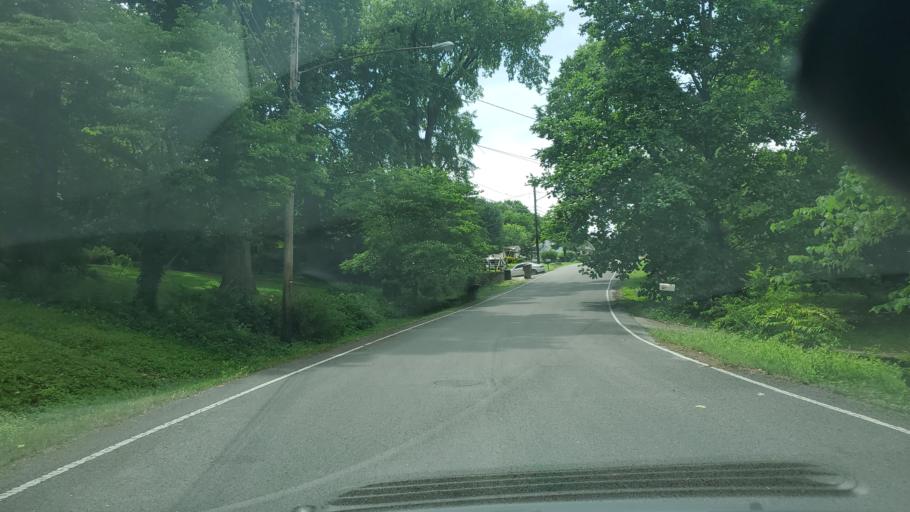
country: US
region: Tennessee
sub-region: Davidson County
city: Oak Hill
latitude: 36.1115
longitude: -86.7149
